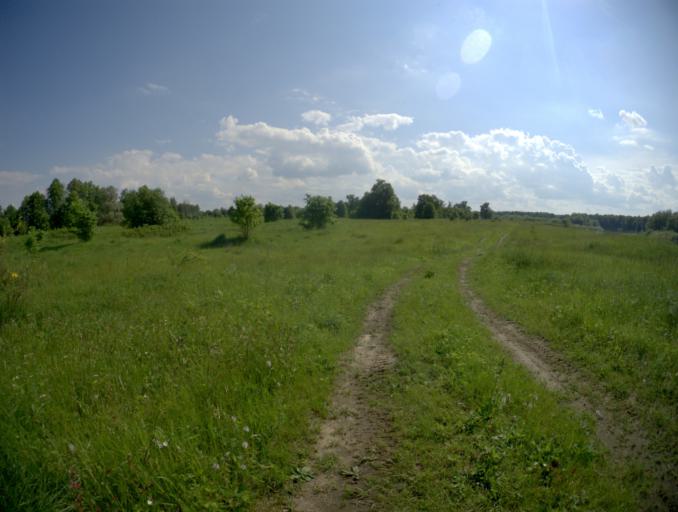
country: RU
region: Vladimir
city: Raduzhnyy
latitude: 56.0501
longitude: 40.2993
